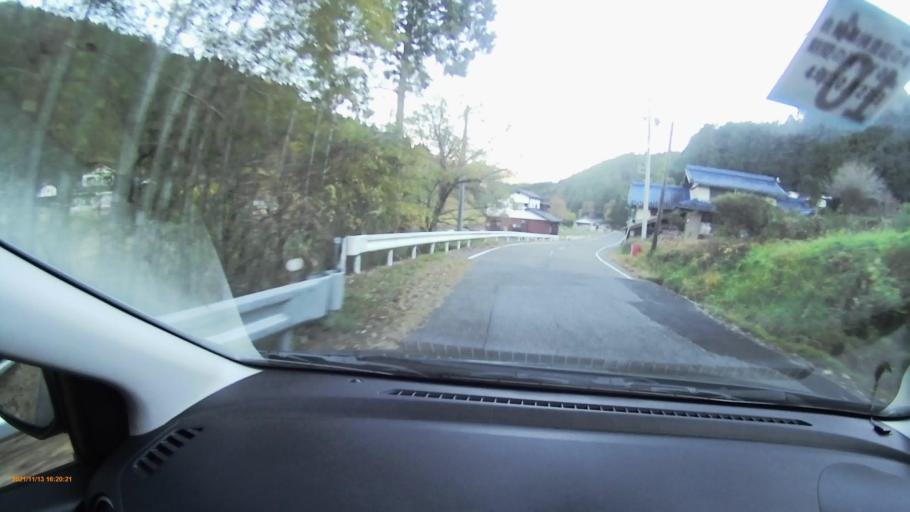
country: JP
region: Gifu
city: Nakatsugawa
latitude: 35.5685
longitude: 137.5157
